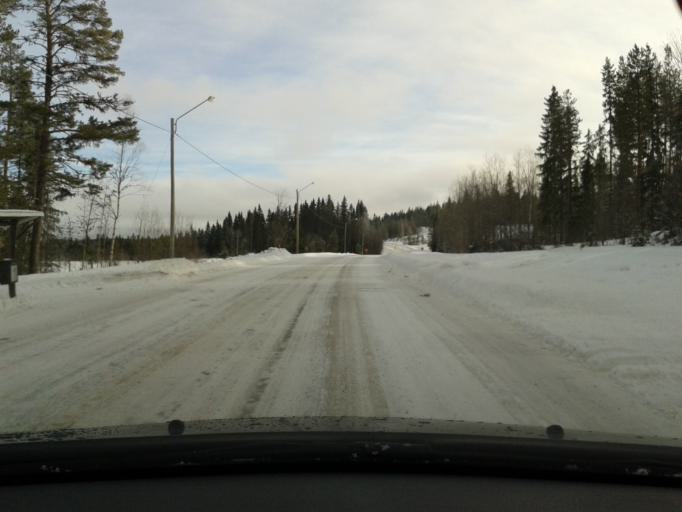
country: SE
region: Vaesterbotten
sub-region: Vilhelmina Kommun
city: Sjoberg
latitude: 64.8001
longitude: 16.0315
